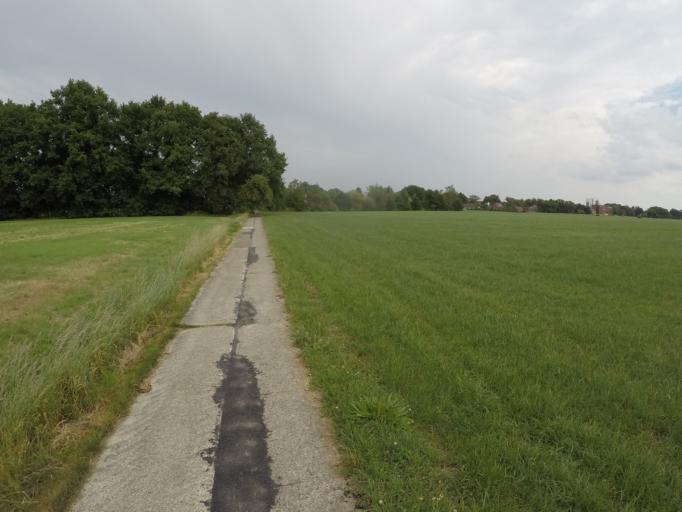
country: BE
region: Flanders
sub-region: Provincie Antwerpen
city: Essen
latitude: 51.4285
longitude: 4.4801
